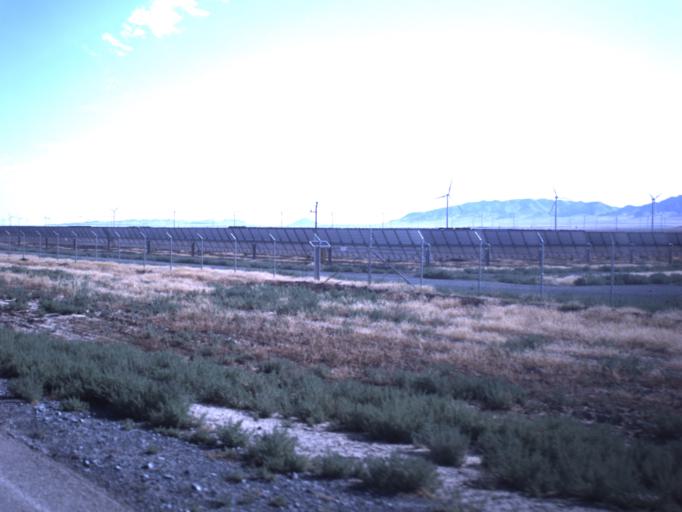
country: US
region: Utah
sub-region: Beaver County
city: Milford
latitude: 38.4949
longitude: -112.9911
